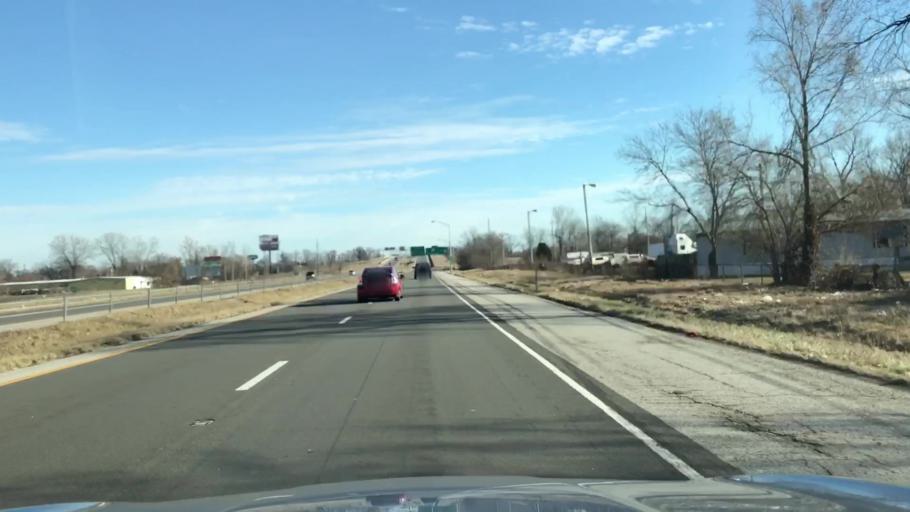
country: US
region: Illinois
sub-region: Madison County
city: Mitchell
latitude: 38.7632
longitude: -90.1045
